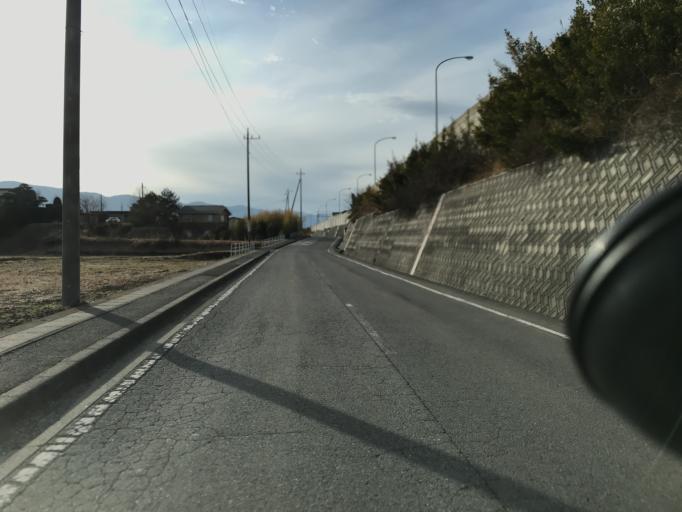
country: JP
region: Nagano
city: Chino
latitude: 35.8686
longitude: 138.3185
